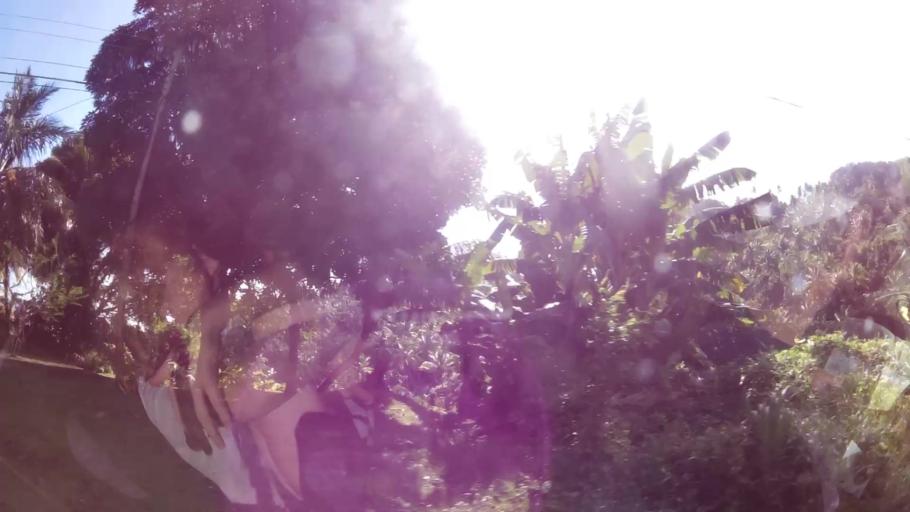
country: DM
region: Saint David
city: Castle Bruce
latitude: 15.4850
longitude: -61.2555
